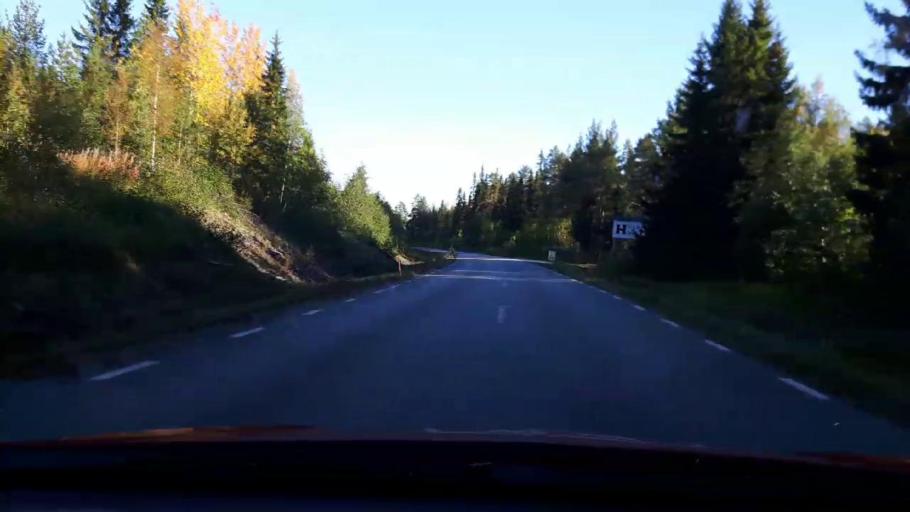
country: SE
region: Jaemtland
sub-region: OEstersunds Kommun
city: Lit
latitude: 63.7516
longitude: 14.7158
